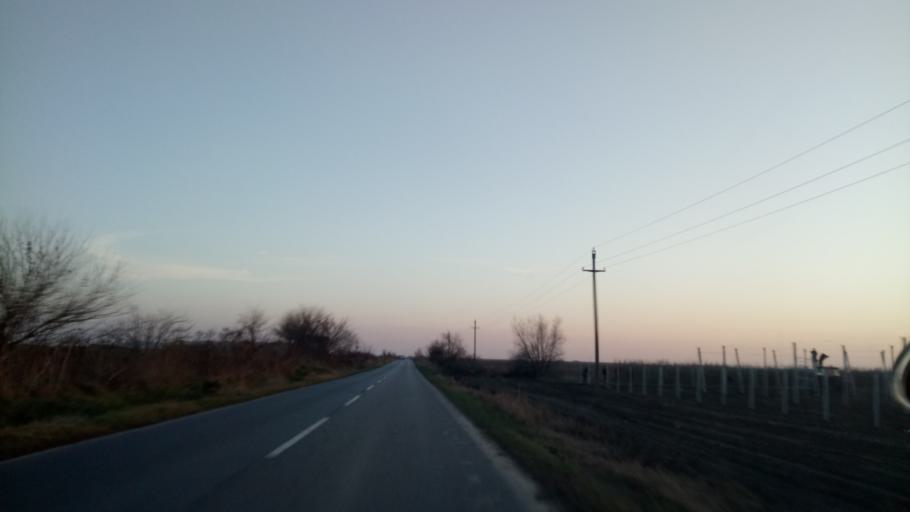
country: RS
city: Belegis
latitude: 45.0446
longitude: 20.3327
